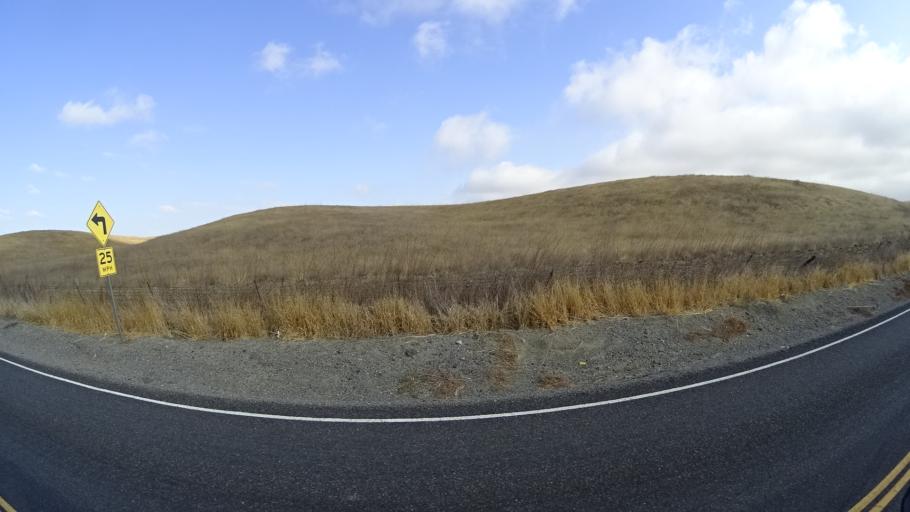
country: US
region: California
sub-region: Yolo County
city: Esparto
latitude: 38.7782
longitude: -121.9645
